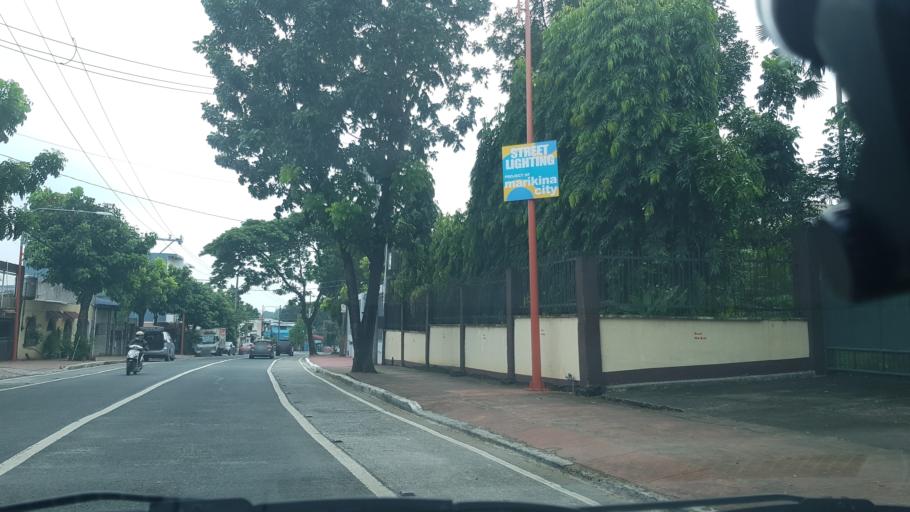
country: PH
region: Calabarzon
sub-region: Province of Rizal
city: Antipolo
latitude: 14.6548
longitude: 121.1227
